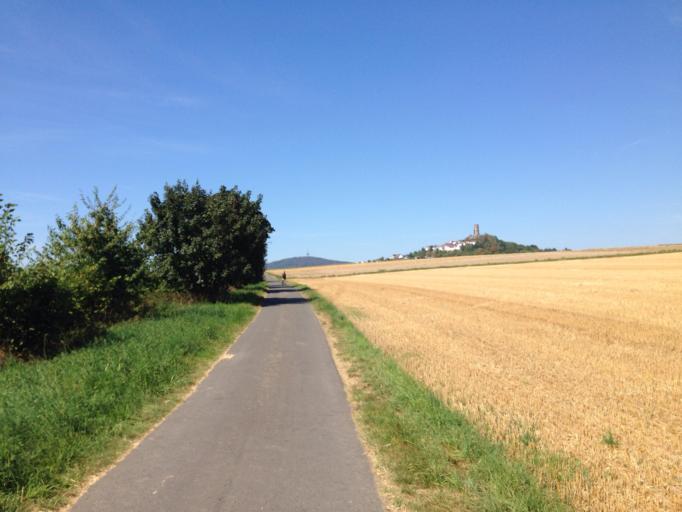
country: DE
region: Hesse
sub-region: Regierungsbezirk Giessen
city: Heuchelheim
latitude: 50.6092
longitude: 8.6226
